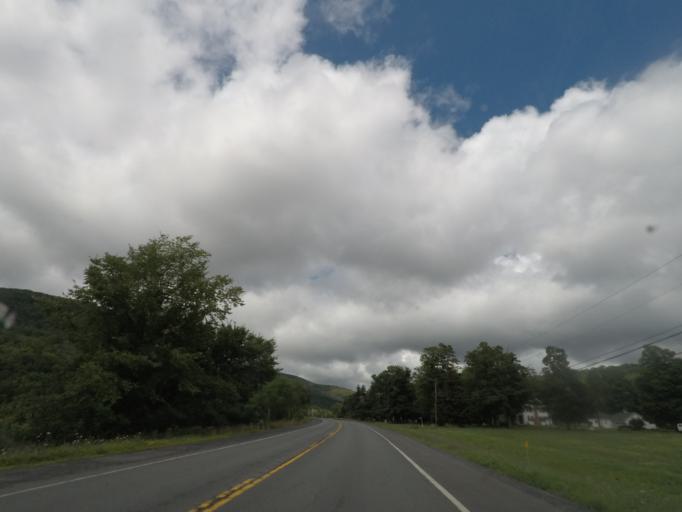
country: US
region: Massachusetts
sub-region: Berkshire County
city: Williamstown
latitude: 42.6467
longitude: -73.3615
